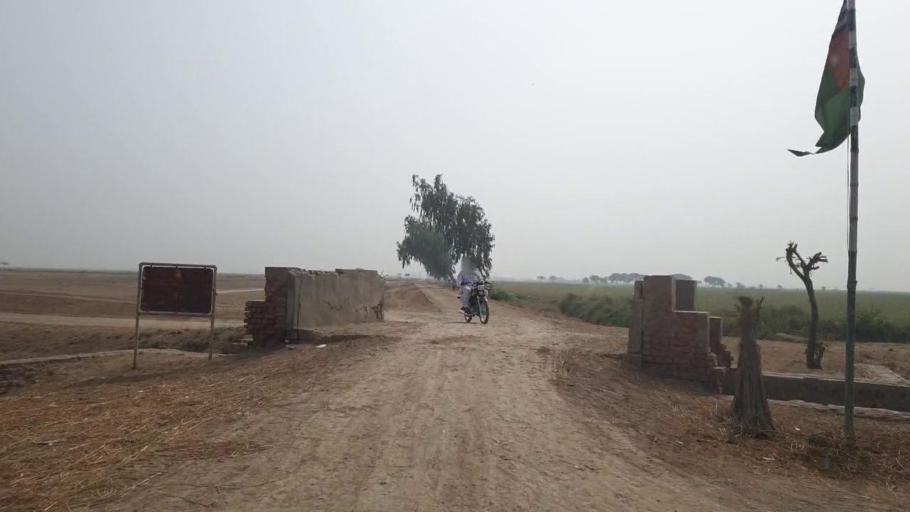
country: PK
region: Sindh
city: Kario
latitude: 24.6317
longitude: 68.5958
